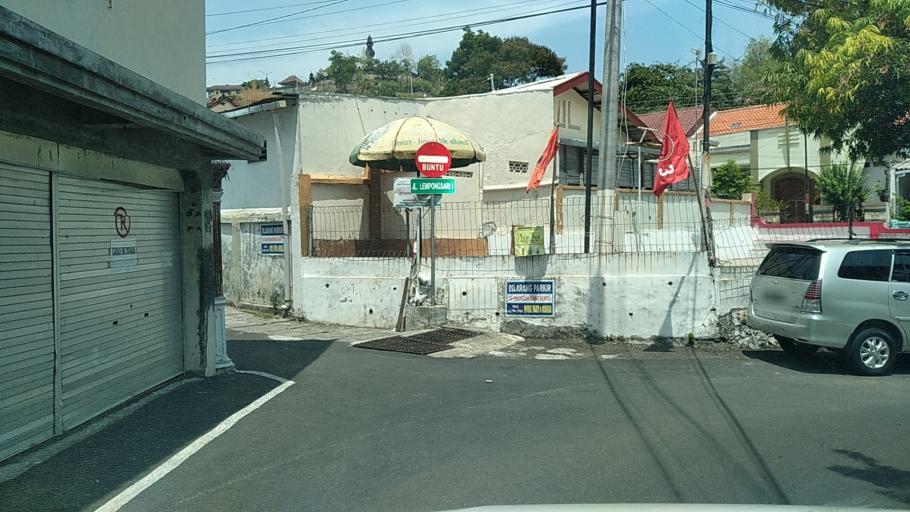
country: ID
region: Central Java
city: Semarang
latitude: -6.9987
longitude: 110.4128
